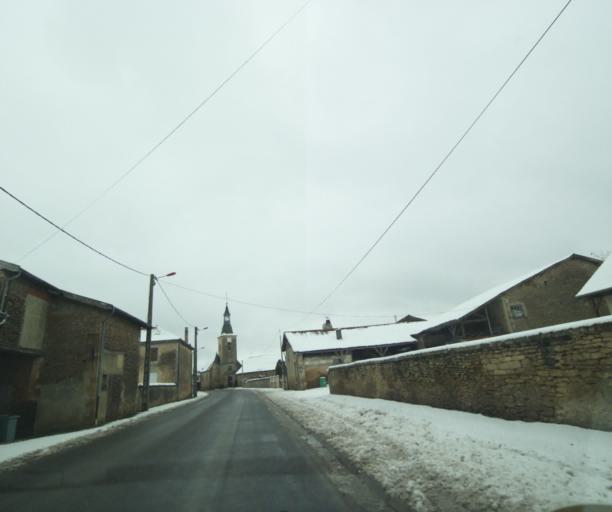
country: FR
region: Champagne-Ardenne
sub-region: Departement de la Haute-Marne
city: Montier-en-Der
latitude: 48.4214
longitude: 4.8188
